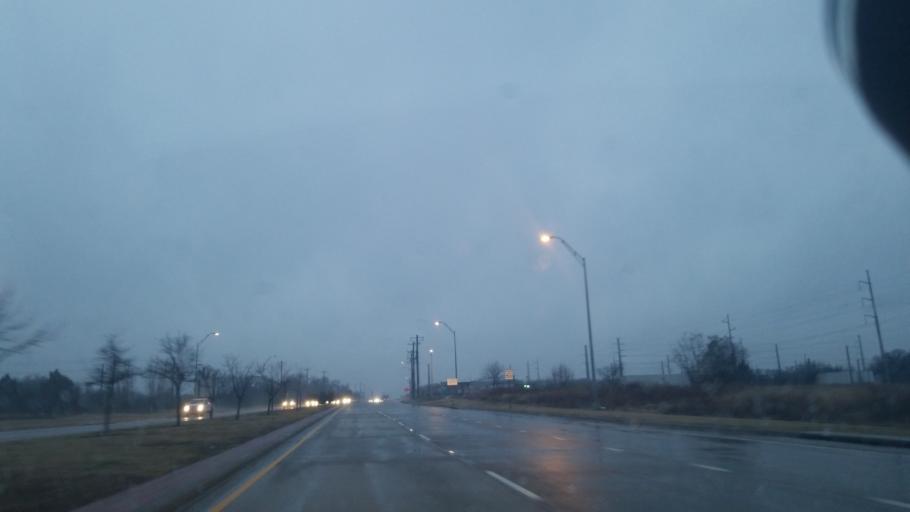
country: US
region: Texas
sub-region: Denton County
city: Denton
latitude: 33.2296
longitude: -97.0899
